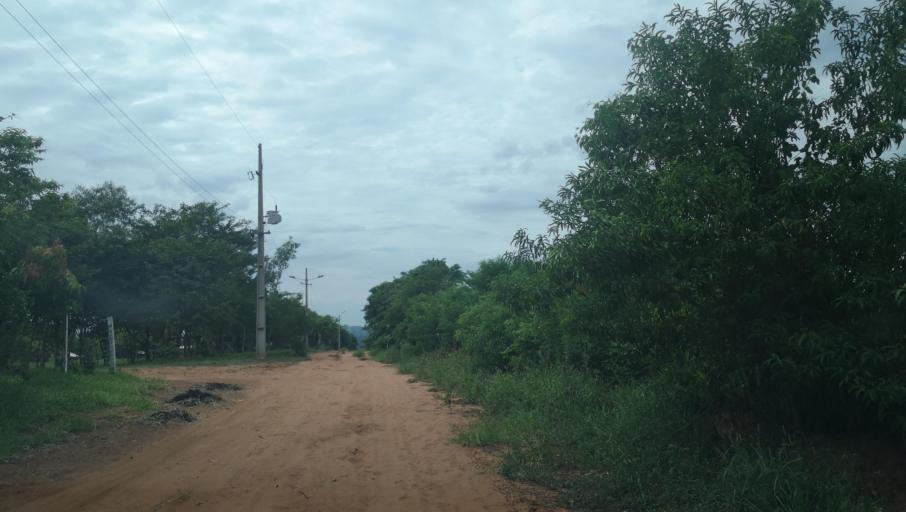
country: PY
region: San Pedro
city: Capiibary
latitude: -24.7204
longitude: -56.0094
